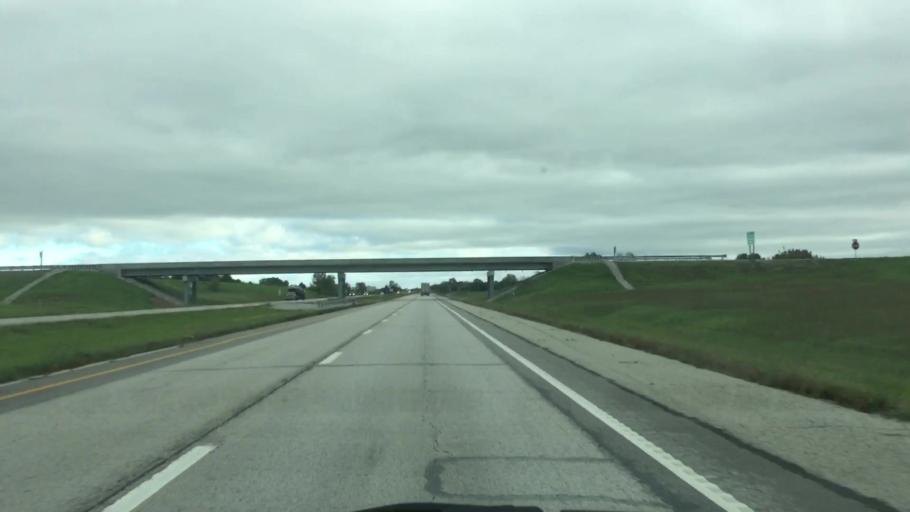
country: US
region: Missouri
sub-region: Harrison County
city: Bethany
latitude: 40.1537
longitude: -94.0338
